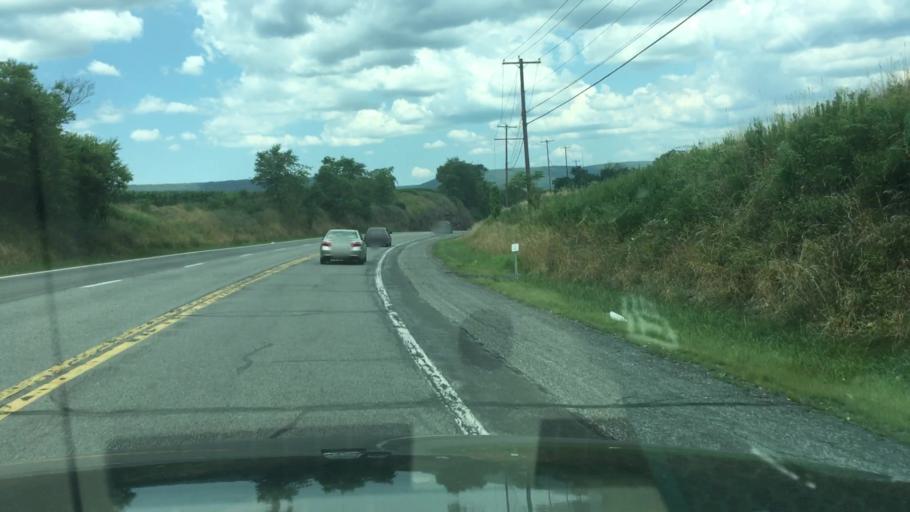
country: US
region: Pennsylvania
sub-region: Northumberland County
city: Mount Carmel
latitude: 40.7339
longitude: -76.3917
